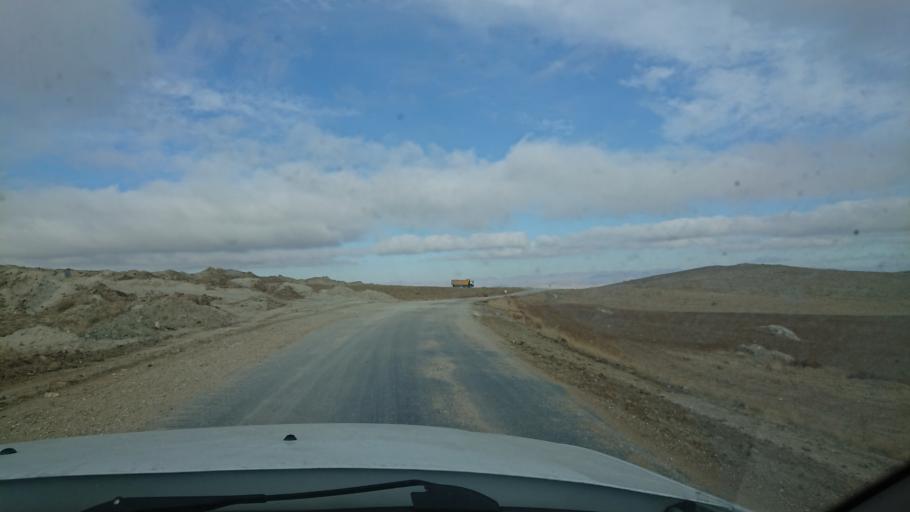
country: TR
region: Aksaray
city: Ortakoy
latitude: 38.7803
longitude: 34.0046
